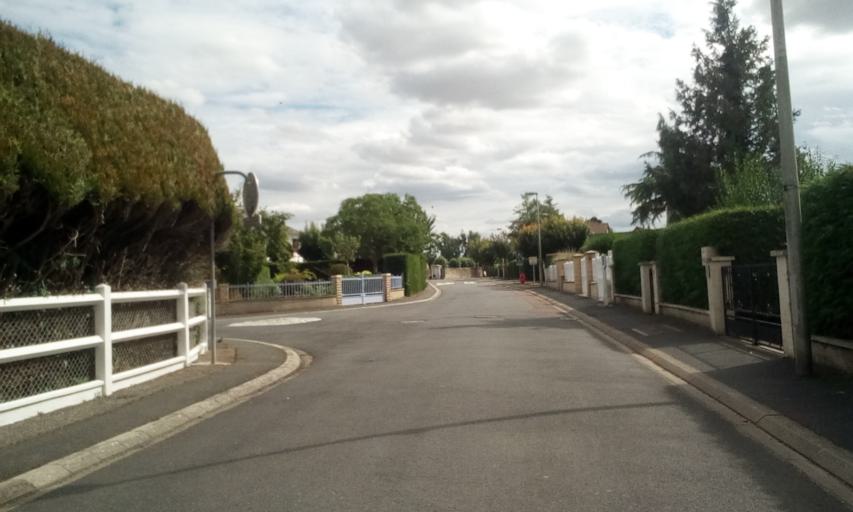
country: FR
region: Lower Normandy
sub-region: Departement du Calvados
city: Bellengreville
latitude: 49.1216
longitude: -0.2000
